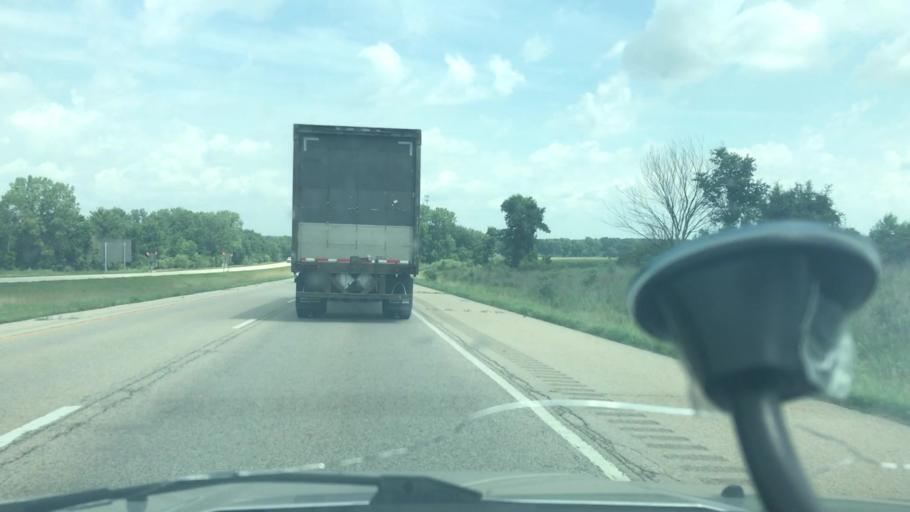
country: US
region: Illinois
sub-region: Peoria County
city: Bellevue
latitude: 40.7109
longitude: -89.6760
